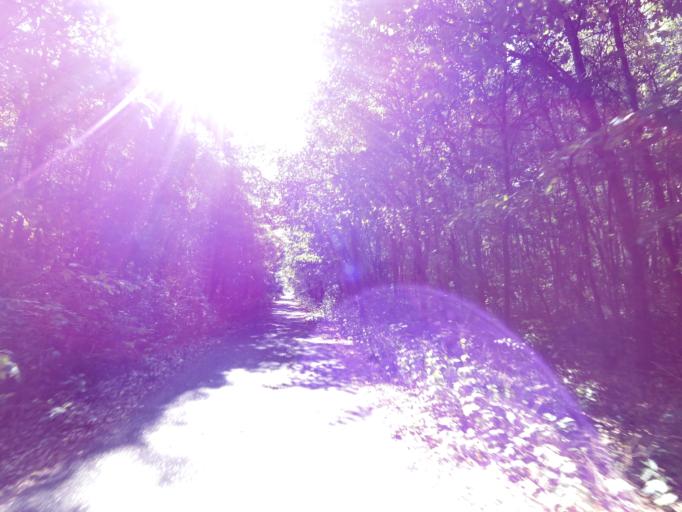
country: DE
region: Berlin
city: Lichtenrade
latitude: 52.3813
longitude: 13.3871
